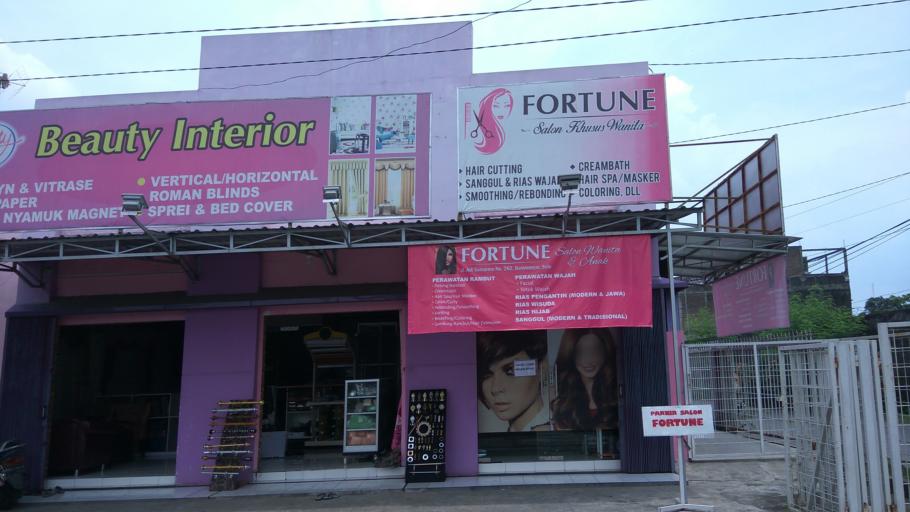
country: ID
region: Central Java
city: Surakarta
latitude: -7.5365
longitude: 110.8012
